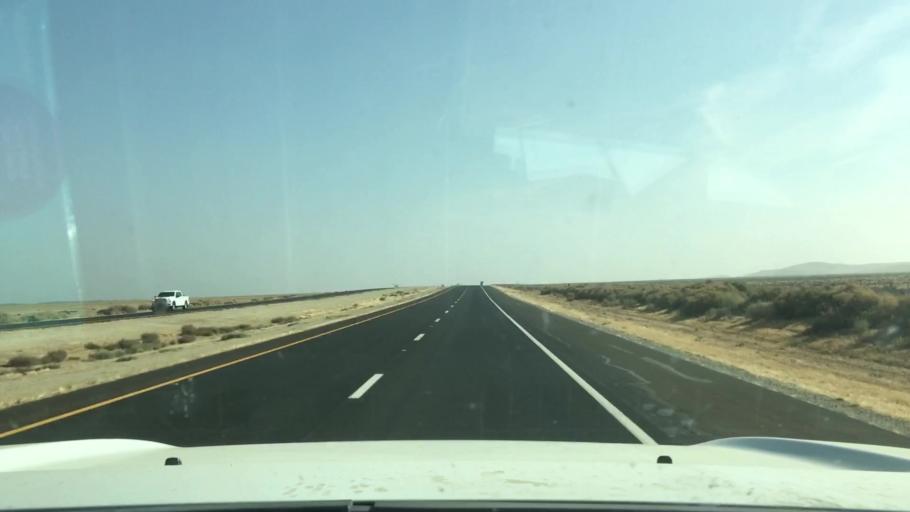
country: US
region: California
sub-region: Kern County
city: Lost Hills
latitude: 35.6355
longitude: -120.0089
